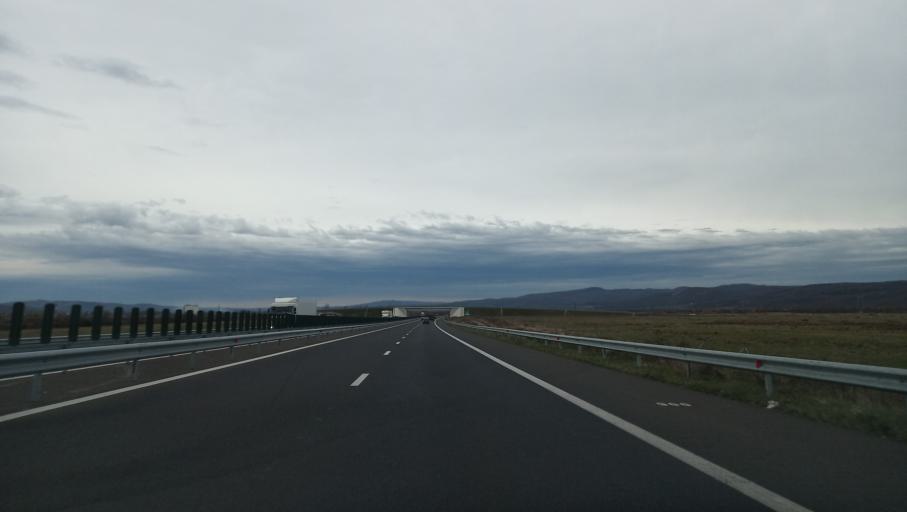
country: RO
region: Hunedoara
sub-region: Comuna Ilia
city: Ilia
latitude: 45.9462
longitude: 22.6891
